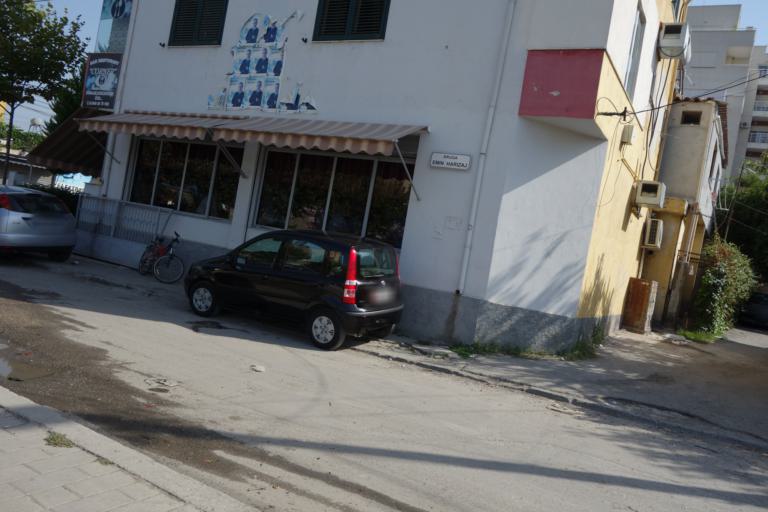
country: AL
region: Tirane
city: Tirana
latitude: 41.3280
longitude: 19.8367
